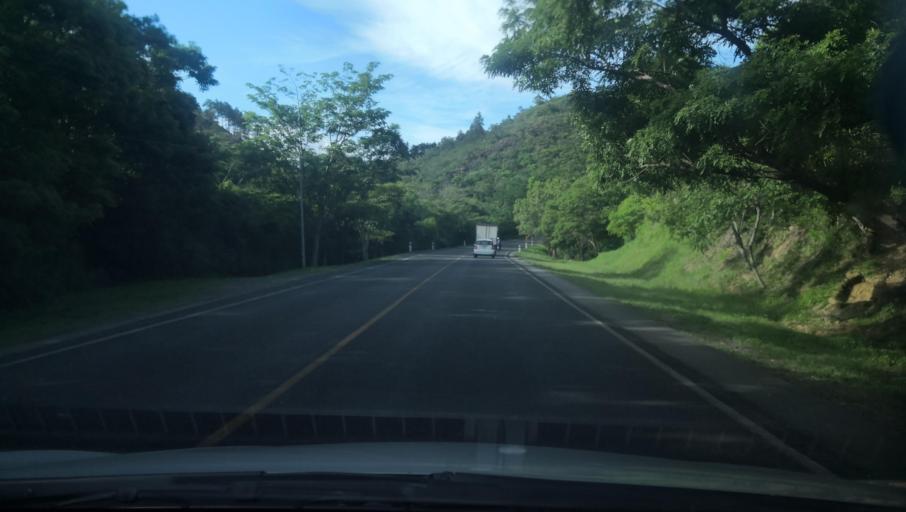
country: NI
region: Madriz
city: Totogalpa
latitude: 13.5669
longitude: -86.4846
